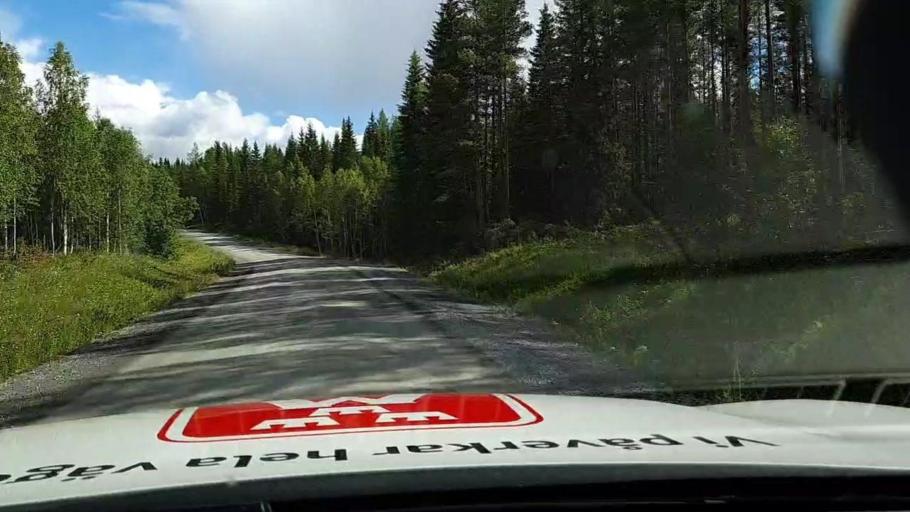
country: SE
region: Jaemtland
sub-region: Krokoms Kommun
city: Valla
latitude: 63.6718
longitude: 13.6982
